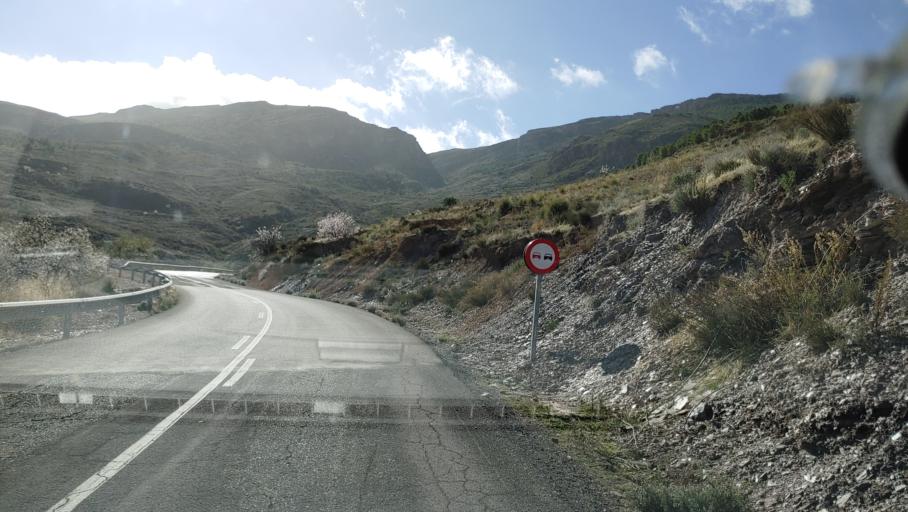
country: ES
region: Andalusia
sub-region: Provincia de Almeria
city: Alicun
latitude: 36.9387
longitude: -2.6043
